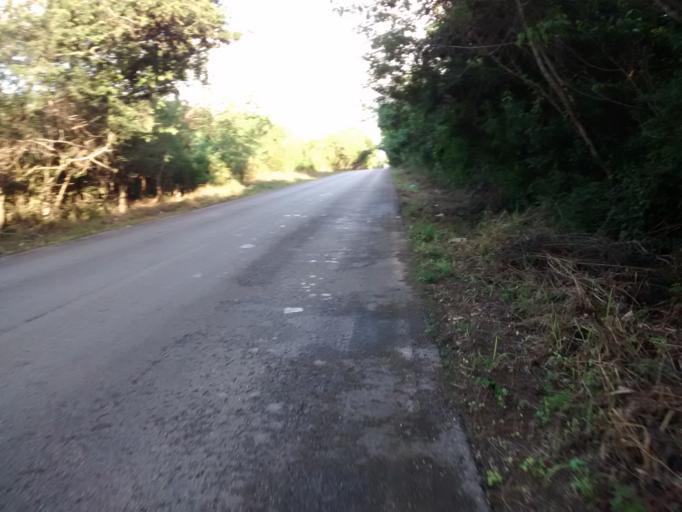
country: MX
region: Yucatan
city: Valladolid
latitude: 20.7311
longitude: -88.2184
